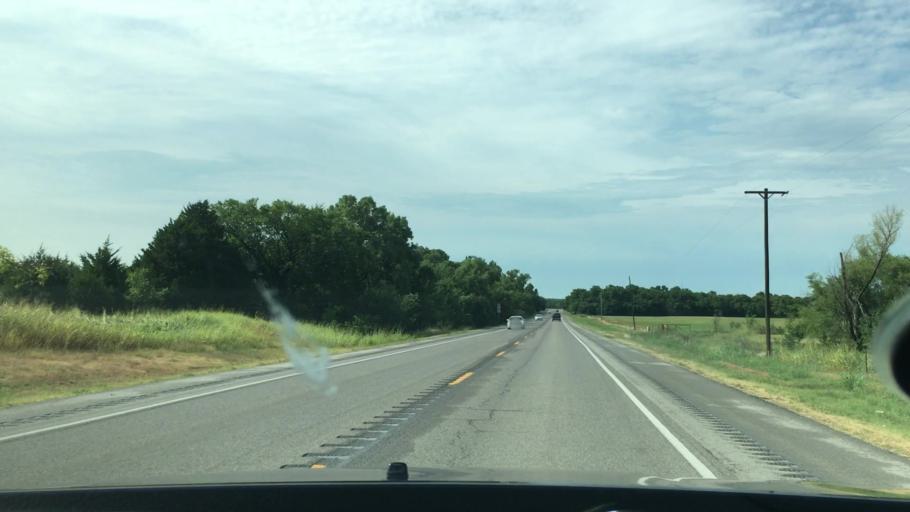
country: US
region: Oklahoma
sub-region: Murray County
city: Sulphur
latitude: 34.5401
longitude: -96.9674
